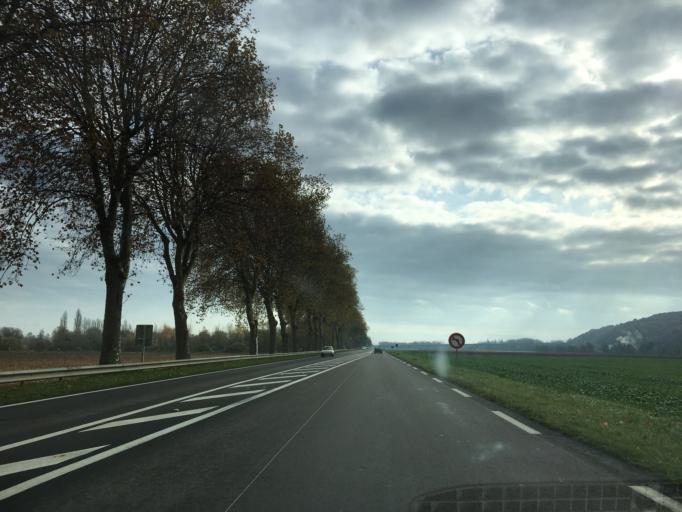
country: FR
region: Bourgogne
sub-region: Departement de l'Yonne
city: Saint-Martin-du-Tertre
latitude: 48.2514
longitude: 3.2462
